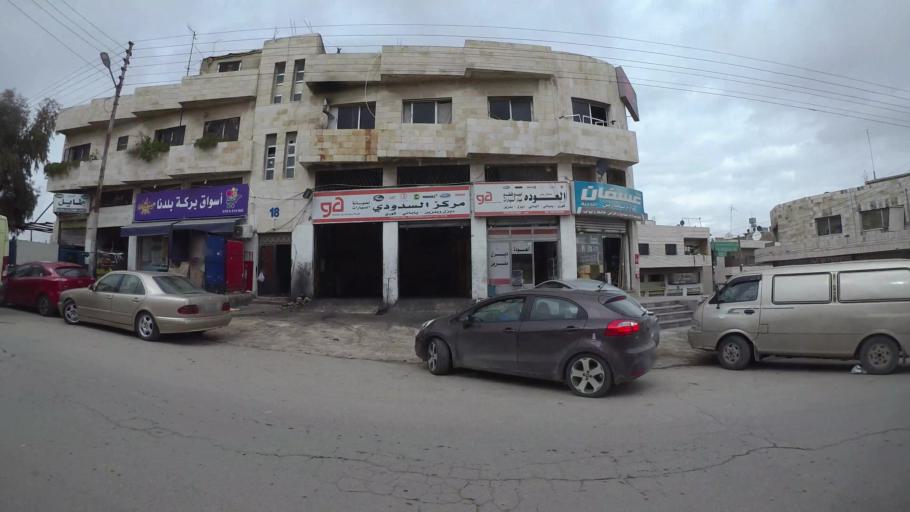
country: JO
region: Amman
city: Wadi as Sir
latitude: 31.9449
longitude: 35.8352
